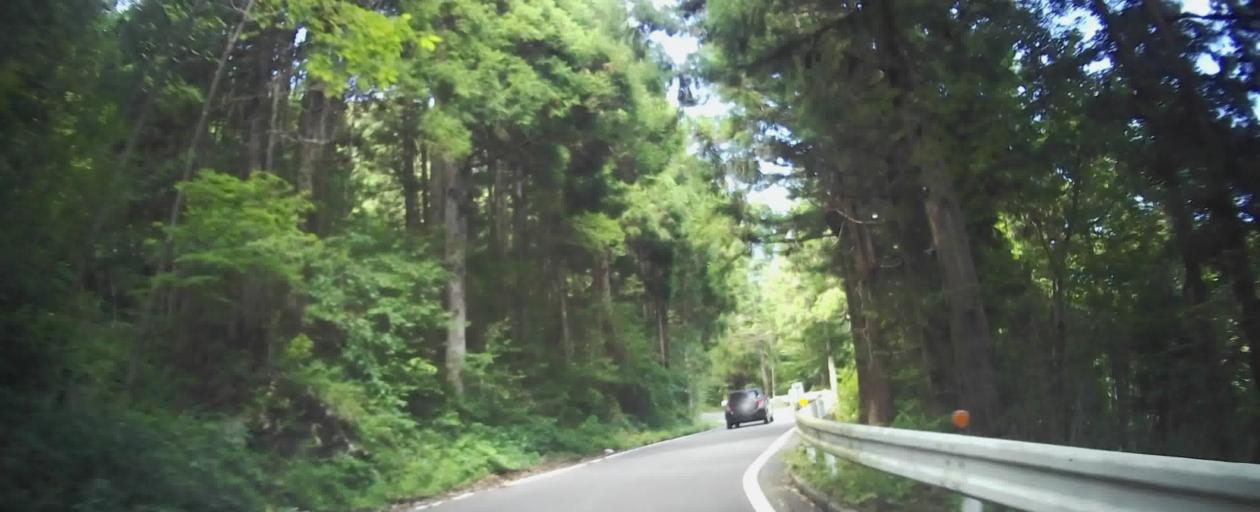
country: JP
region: Gunma
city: Shibukawa
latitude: 36.4595
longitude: 138.8967
